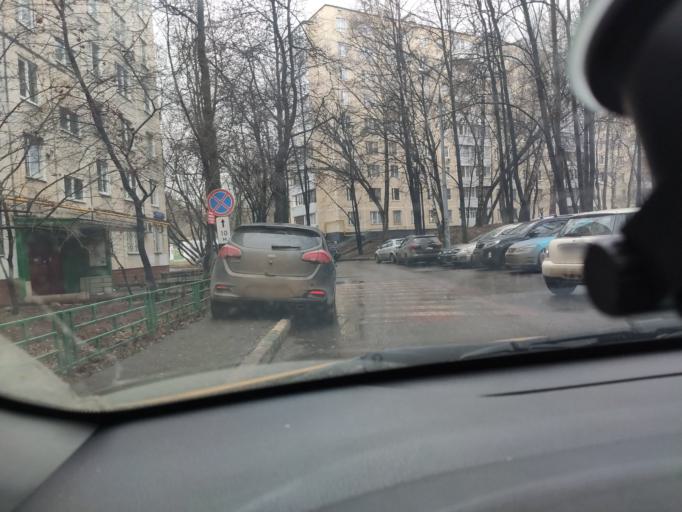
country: RU
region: Moscow
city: Chertanovo Yuzhnoye
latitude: 55.6097
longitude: 37.5988
